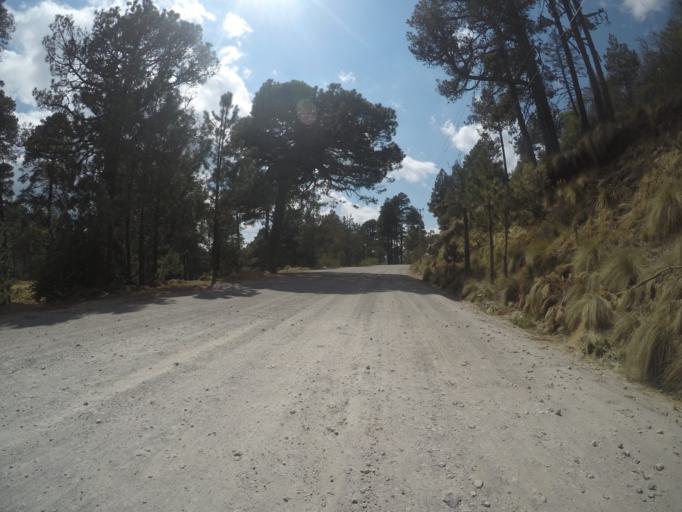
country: MX
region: Mexico
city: Cerro La Calera
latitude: 19.1332
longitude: -99.7920
